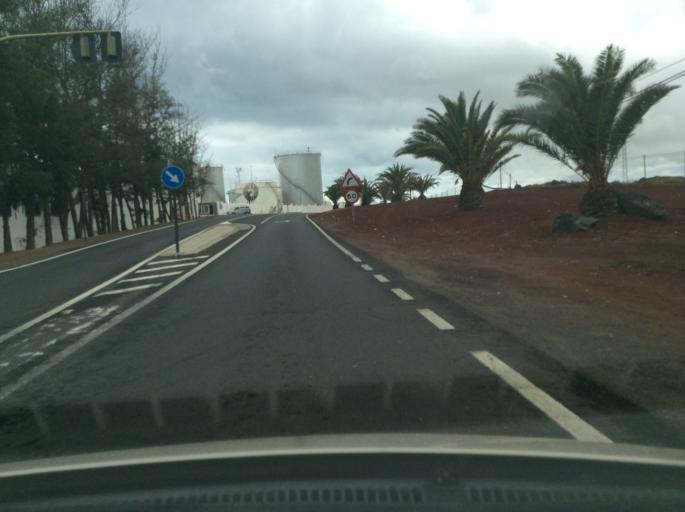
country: ES
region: Canary Islands
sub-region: Provincia de Las Palmas
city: Arrecife
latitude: 28.9788
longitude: -13.5198
